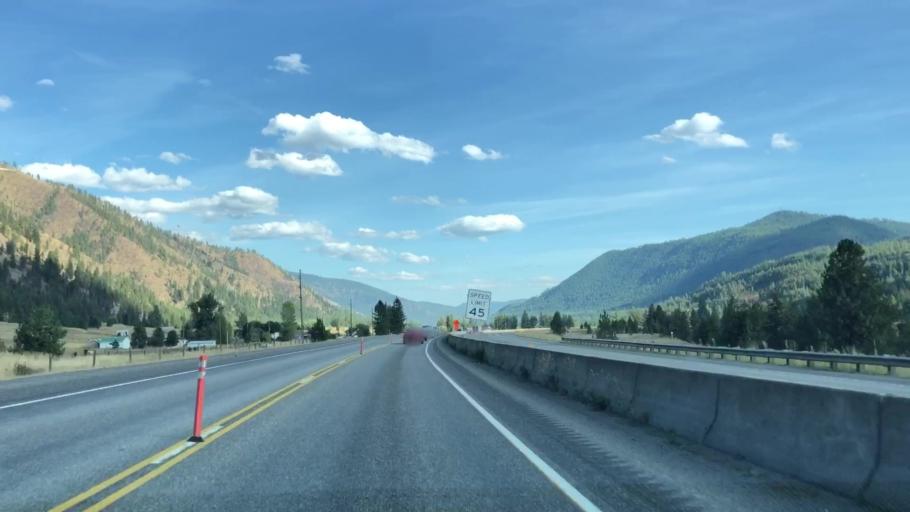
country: US
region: Montana
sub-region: Mineral County
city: Superior
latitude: 47.2150
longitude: -114.9451
